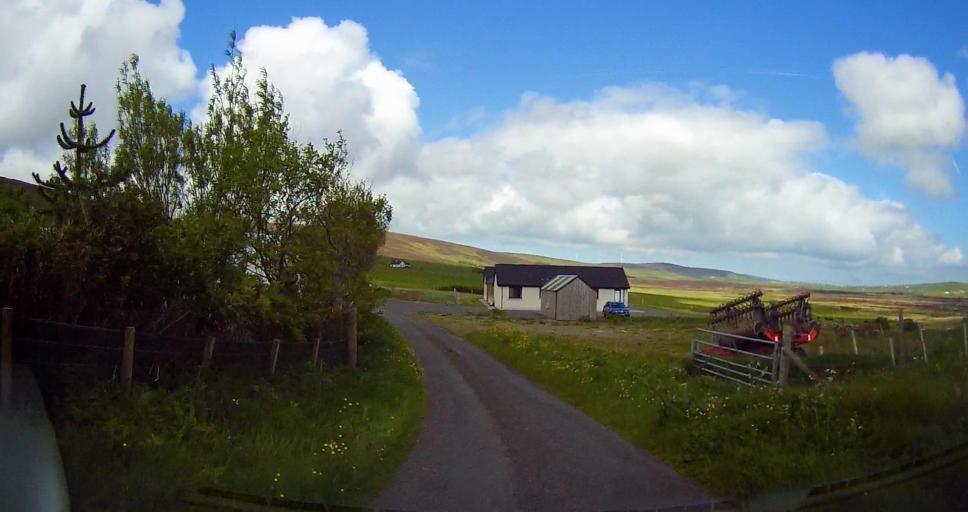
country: GB
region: Scotland
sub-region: Orkney Islands
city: Orkney
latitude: 59.0509
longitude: -3.1028
